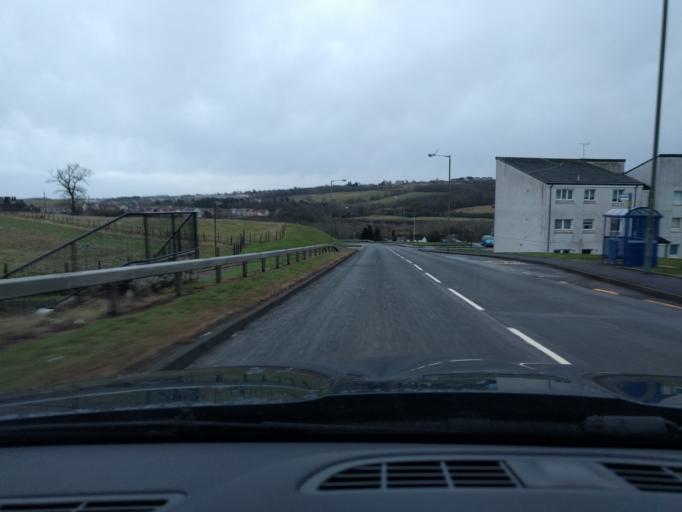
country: GB
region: Scotland
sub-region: Falkirk
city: Falkirk
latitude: 55.9874
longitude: -3.7663
